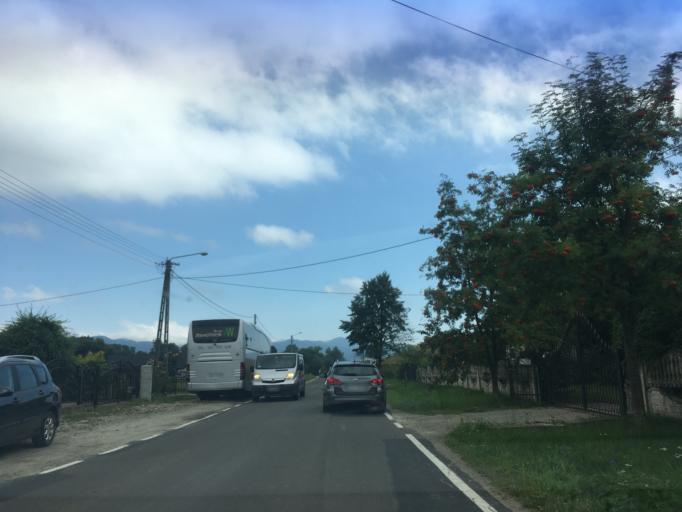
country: PL
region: Lesser Poland Voivodeship
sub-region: Powiat nowotarski
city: Frydman
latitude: 49.4384
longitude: 20.1771
